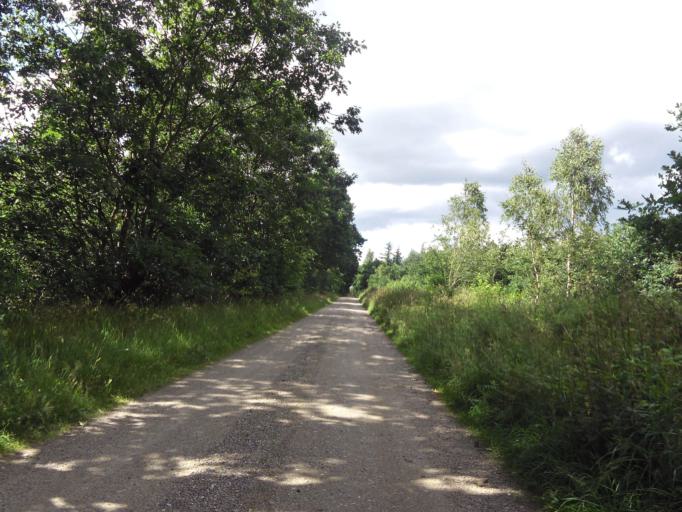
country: DK
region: South Denmark
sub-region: Haderslev Kommune
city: Vojens
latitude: 55.3235
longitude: 9.1956
